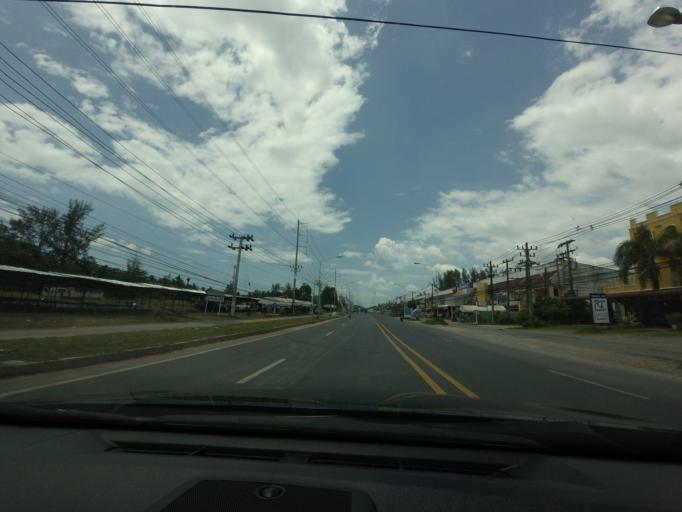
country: TH
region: Phangnga
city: Ban Khao Lak
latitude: 8.6628
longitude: 98.2533
